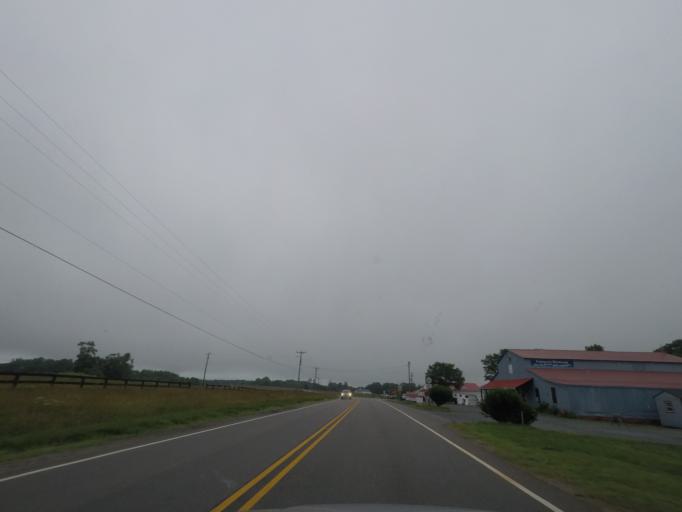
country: US
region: Virginia
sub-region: Fluvanna County
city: Weber City
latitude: 37.6128
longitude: -78.3808
